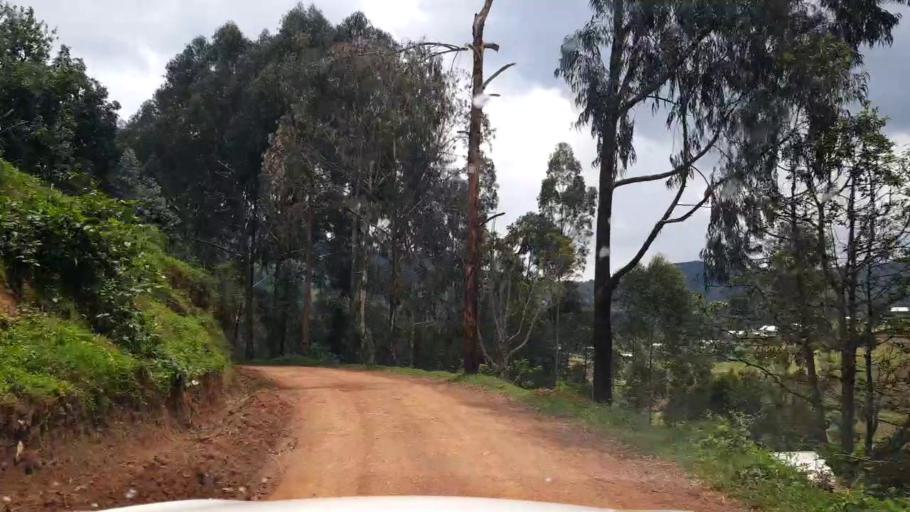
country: UG
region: Western Region
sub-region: Kabale District
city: Kabale
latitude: -1.4327
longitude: 29.8667
